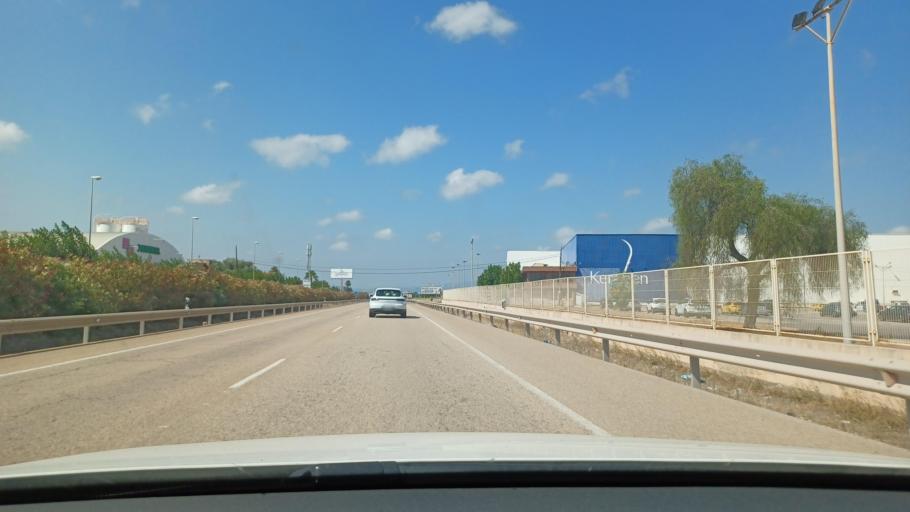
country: ES
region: Valencia
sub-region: Provincia de Castello
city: Moncofar
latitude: 39.8270
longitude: -0.1651
